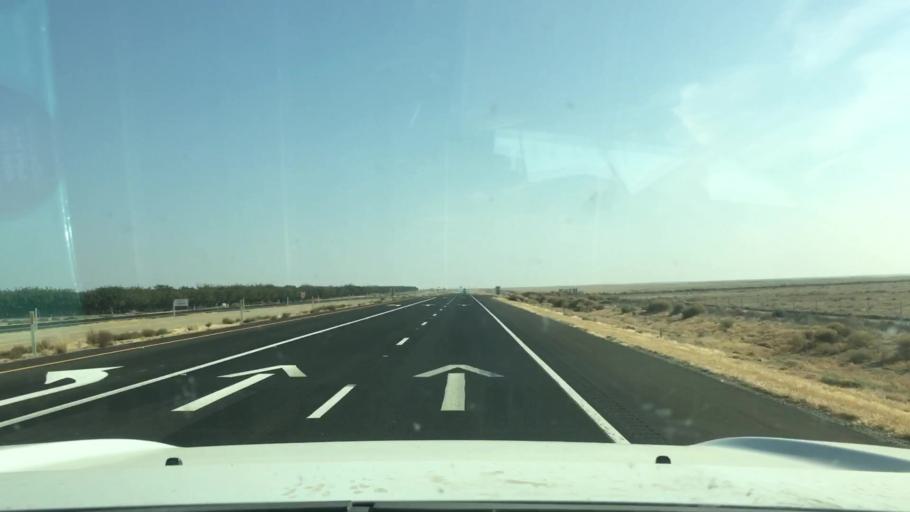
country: US
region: California
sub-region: Kern County
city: Lost Hills
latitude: 35.6202
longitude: -119.9767
